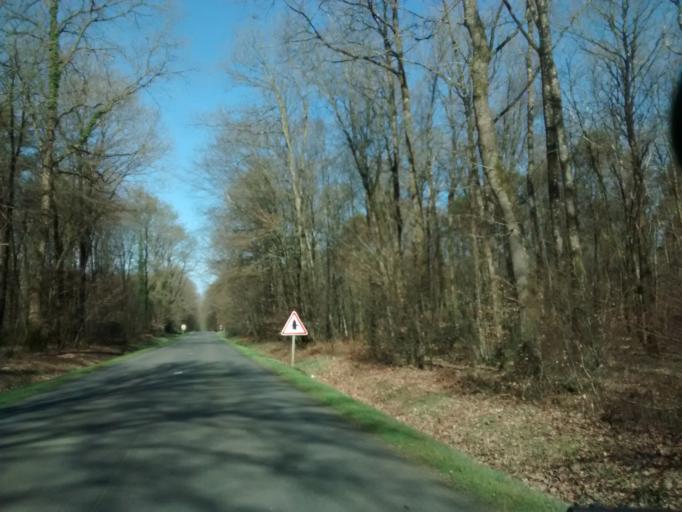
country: FR
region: Brittany
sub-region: Departement d'Ille-et-Vilaine
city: Liffre
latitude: 48.2069
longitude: -1.5431
